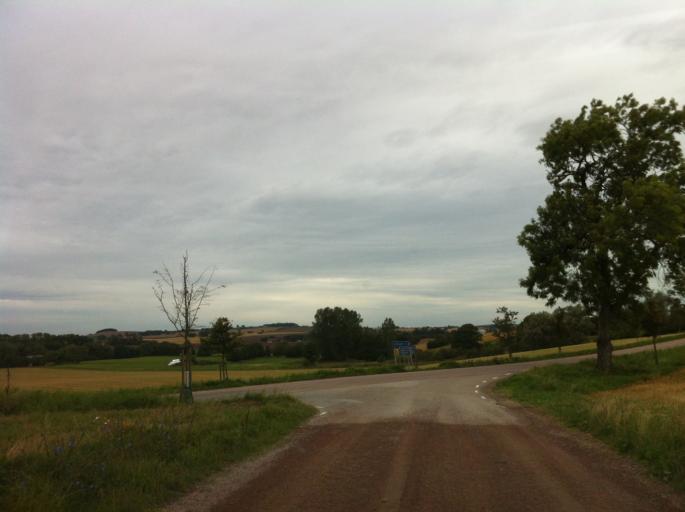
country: SE
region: Skane
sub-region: Landskrona
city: Asmundtorp
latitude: 55.9305
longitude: 12.9904
